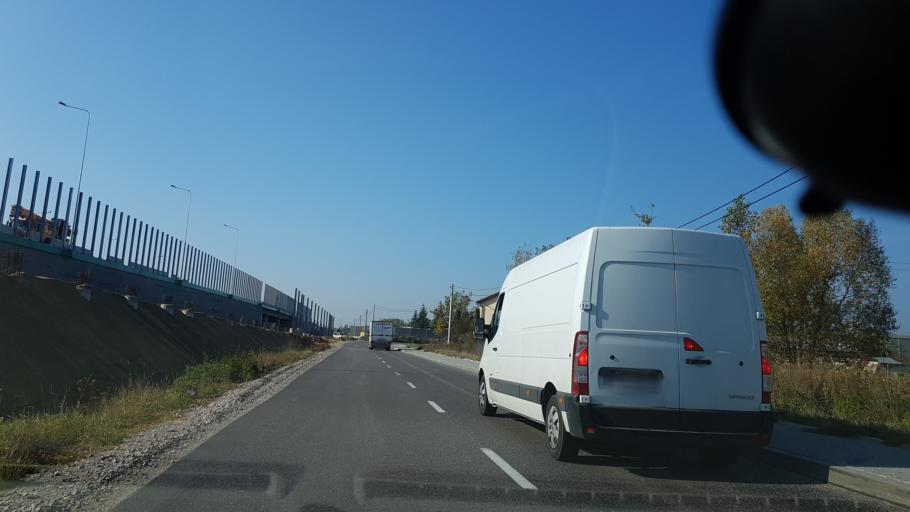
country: PL
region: Masovian Voivodeship
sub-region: Powiat pruszkowski
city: Nadarzyn
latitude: 52.0754
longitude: 20.7758
